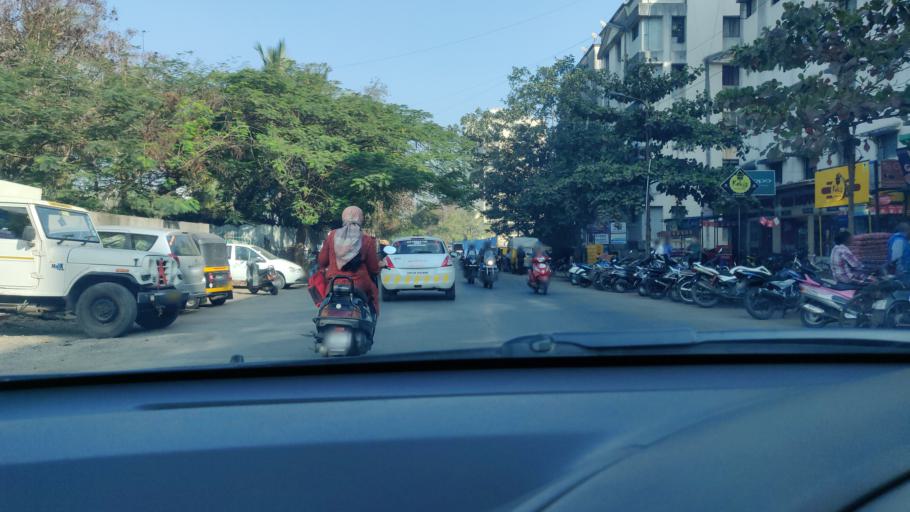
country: IN
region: Maharashtra
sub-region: Pune Division
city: Khadki
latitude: 18.5621
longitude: 73.8028
